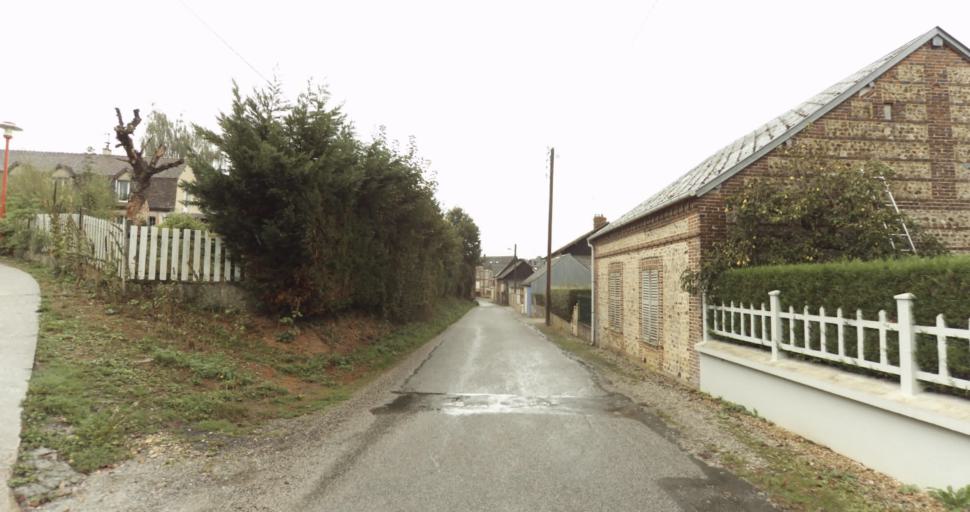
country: FR
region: Lower Normandy
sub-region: Departement de l'Orne
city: Sainte-Gauburge-Sainte-Colombe
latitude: 48.7130
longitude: 0.4313
